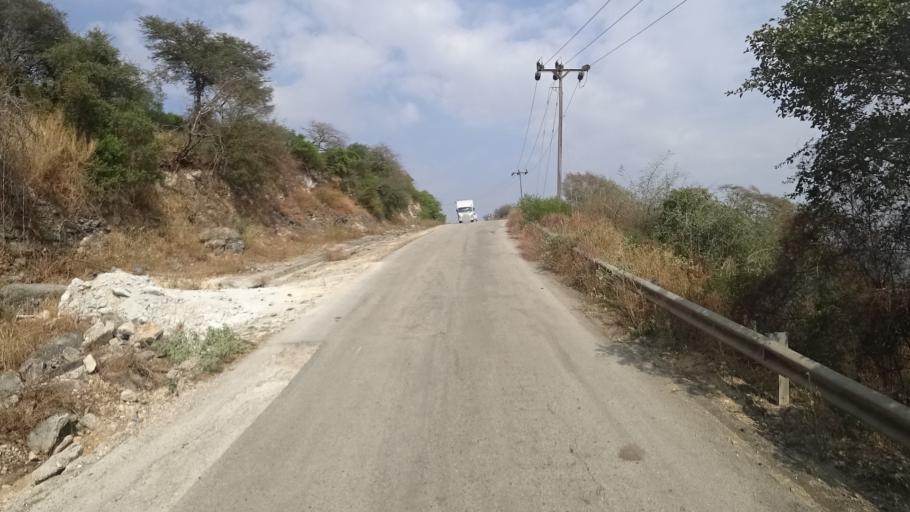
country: YE
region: Al Mahrah
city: Hawf
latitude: 16.7260
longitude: 53.2745
